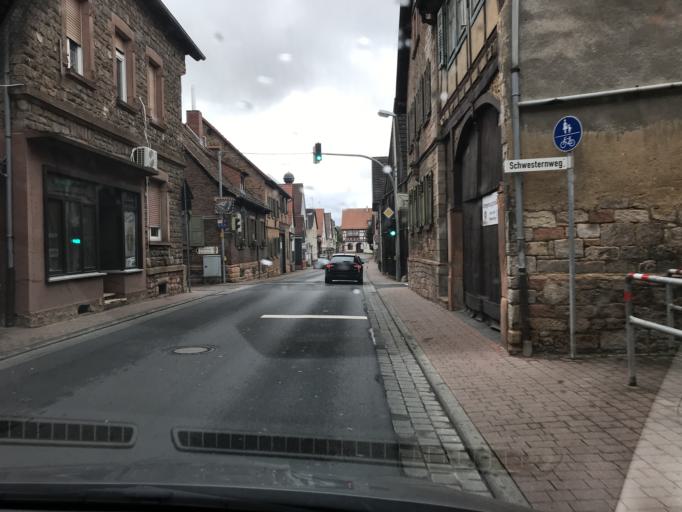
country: DE
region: Bavaria
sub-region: Regierungsbezirk Unterfranken
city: Grossostheim
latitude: 49.9102
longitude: 9.0606
